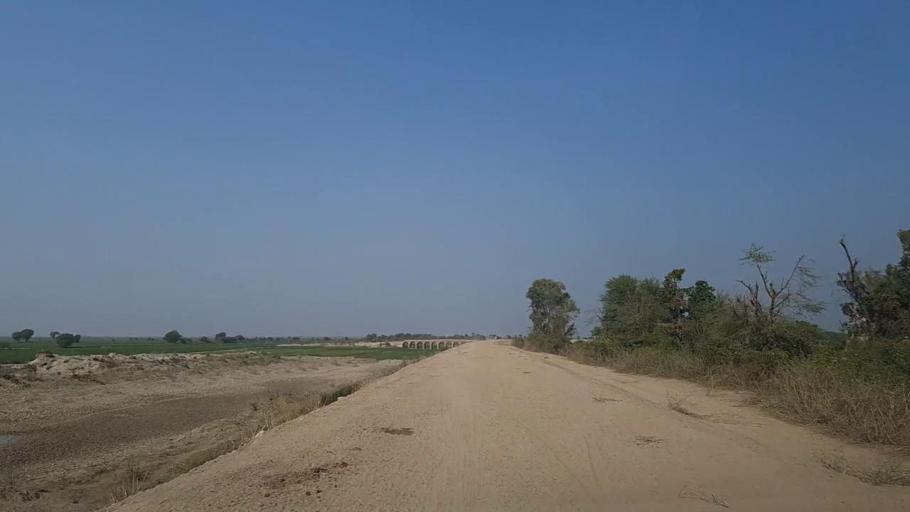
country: PK
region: Sindh
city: Naushahro Firoz
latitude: 26.8509
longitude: 67.9583
